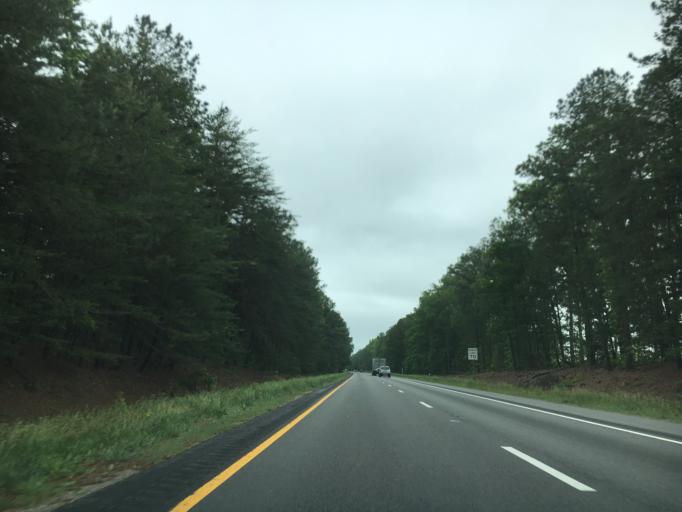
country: US
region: Virginia
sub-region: Dinwiddie County
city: Dinwiddie
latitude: 37.0282
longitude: -77.6410
